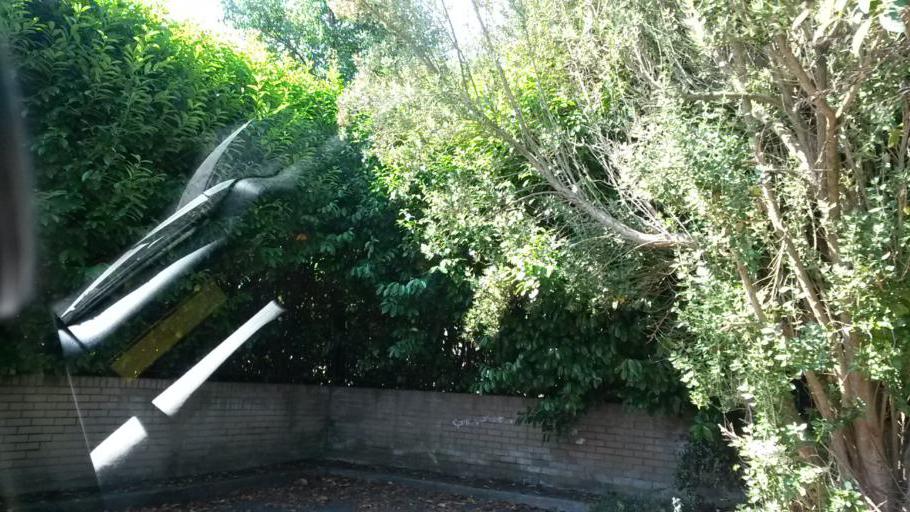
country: IE
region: Leinster
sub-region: Fingal County
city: Swords
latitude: 53.4467
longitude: -6.2422
